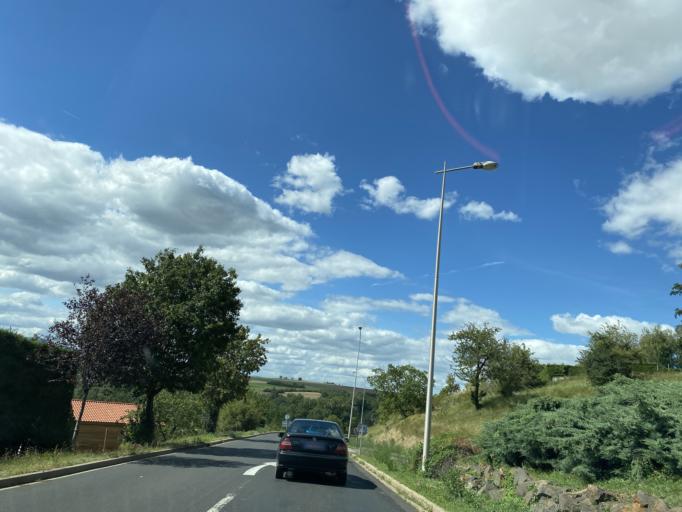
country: FR
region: Auvergne
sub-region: Departement du Puy-de-Dome
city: Dallet
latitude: 45.7708
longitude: 3.2409
